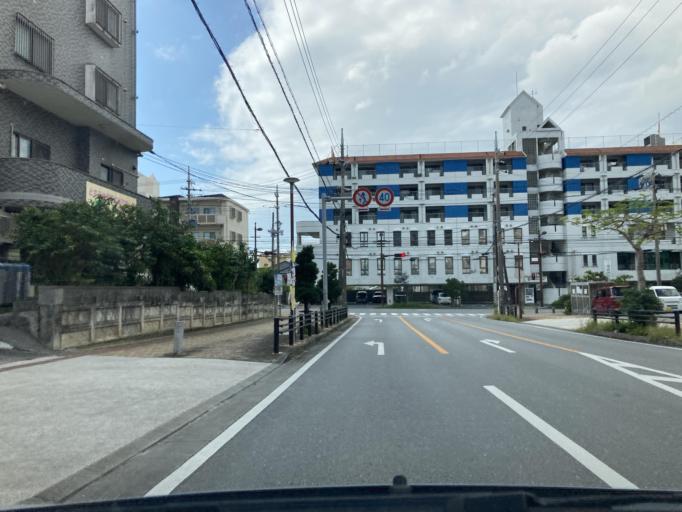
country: JP
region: Okinawa
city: Ginowan
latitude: 26.2506
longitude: 127.7725
